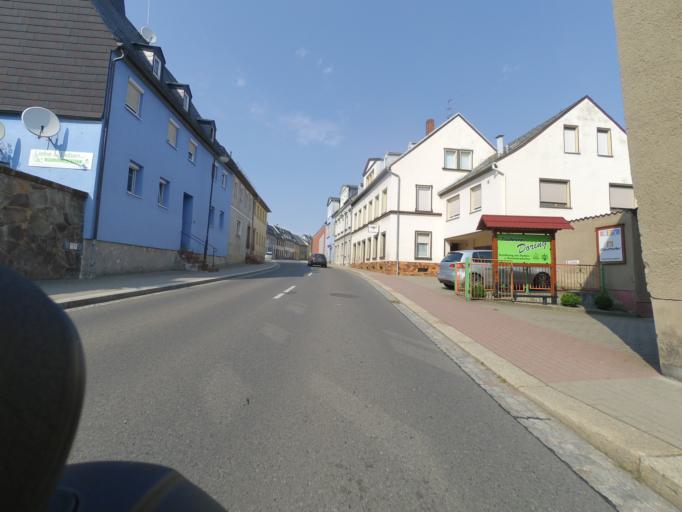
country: DE
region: Saxony
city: Geringswalde
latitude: 51.0751
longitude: 12.8997
